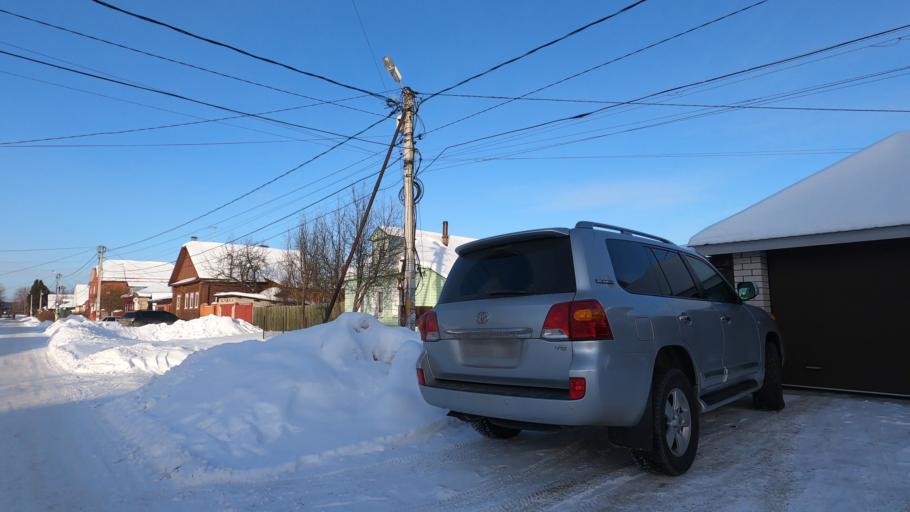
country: RU
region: Moskovskaya
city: Pavlovskiy Posad
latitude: 55.7703
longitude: 38.6979
